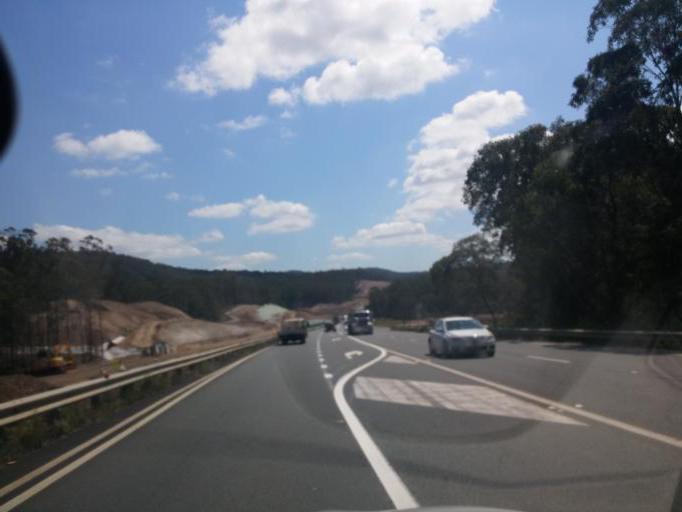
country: AU
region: New South Wales
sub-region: Port Macquarie-Hastings
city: North Shore
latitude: -31.2778
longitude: 152.8129
